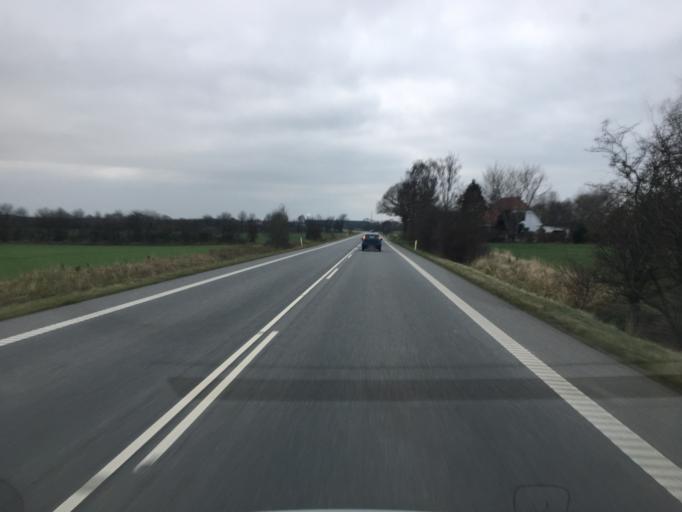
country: DK
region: South Denmark
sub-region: Aabenraa Kommune
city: Rodekro
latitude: 55.0263
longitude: 9.3412
